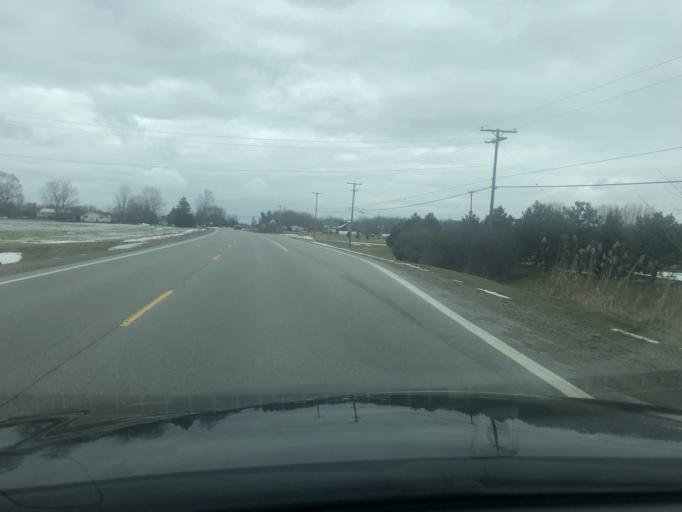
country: US
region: Michigan
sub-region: Saint Clair County
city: Saint Clair
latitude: 42.8153
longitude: -82.5712
